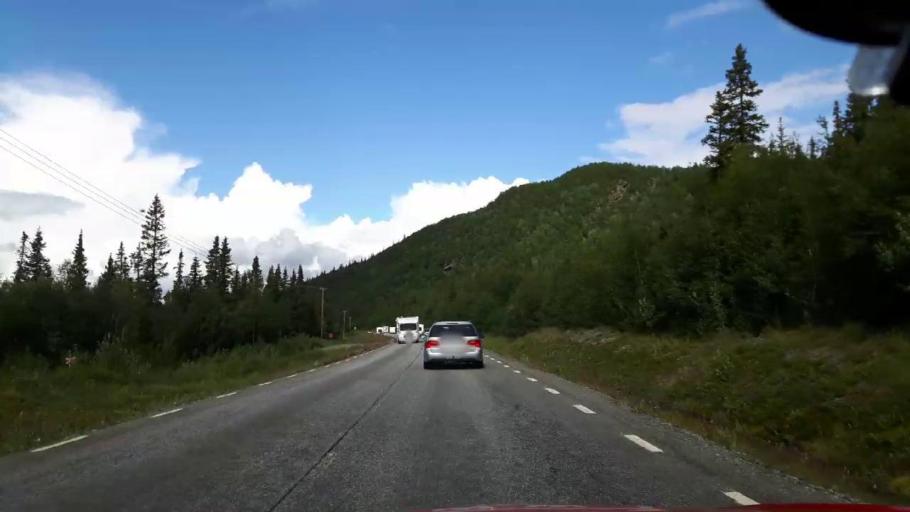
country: SE
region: Vaesterbotten
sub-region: Vilhelmina Kommun
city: Sjoberg
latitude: 65.0350
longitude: 15.1370
